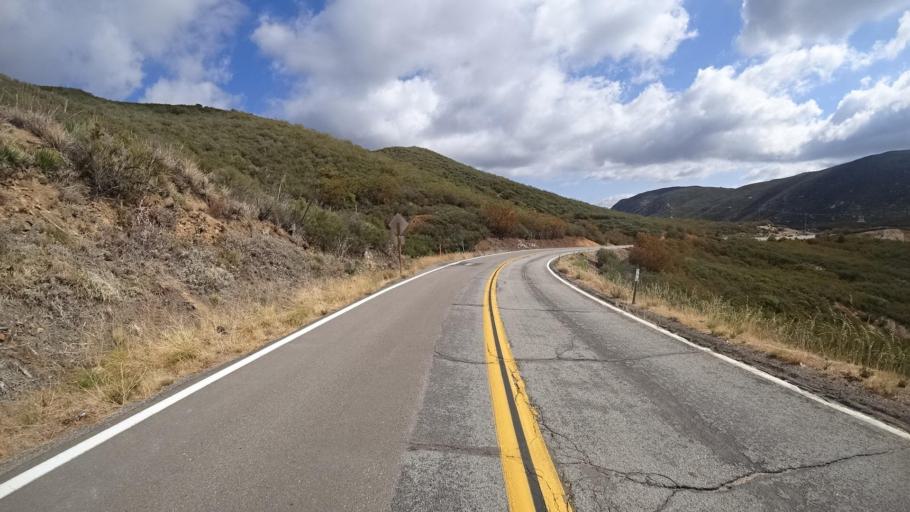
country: US
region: California
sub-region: San Diego County
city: Pine Valley
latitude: 32.8156
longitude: -116.5089
